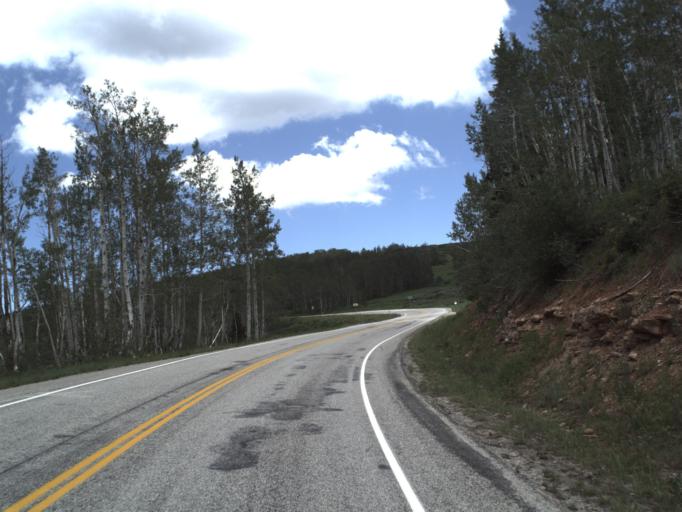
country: US
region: Utah
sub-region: Weber County
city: Wolf Creek
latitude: 41.4137
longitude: -111.5248
